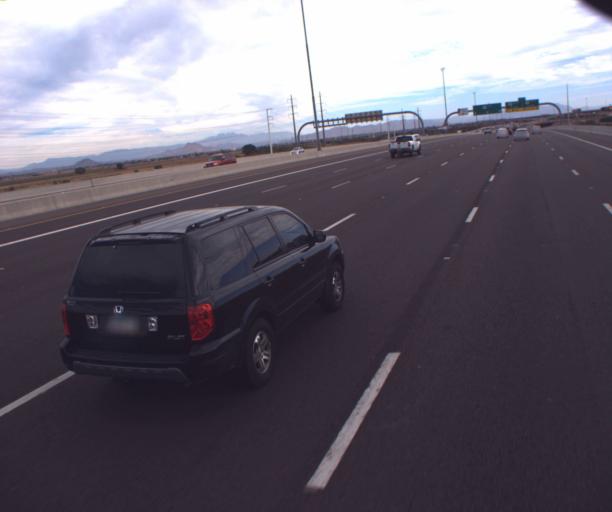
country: US
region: Arizona
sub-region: Maricopa County
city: Tempe
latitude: 33.4358
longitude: -111.9101
